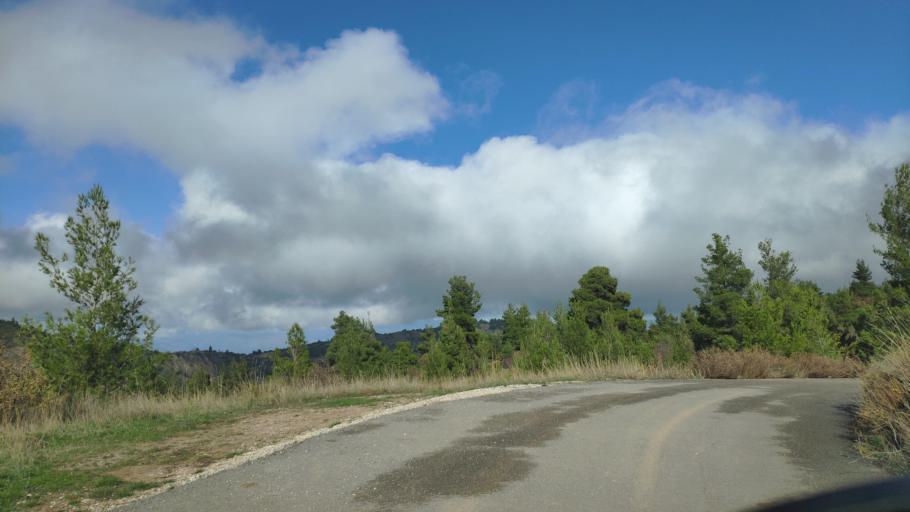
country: GR
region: West Greece
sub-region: Nomos Achaias
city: Aiyira
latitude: 38.0729
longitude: 22.4678
